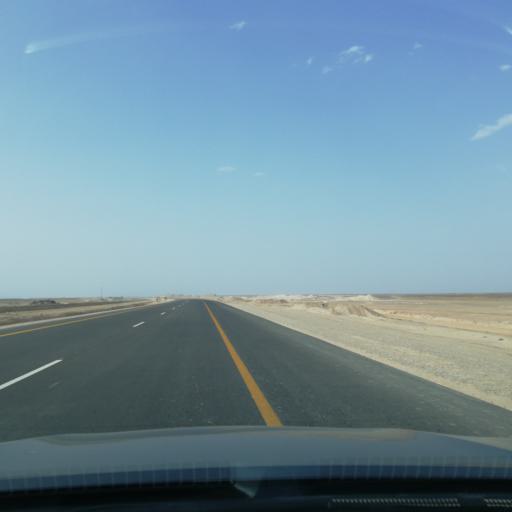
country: OM
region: Muhafazat ad Dakhiliyah
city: Adam
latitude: 22.1207
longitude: 57.5247
